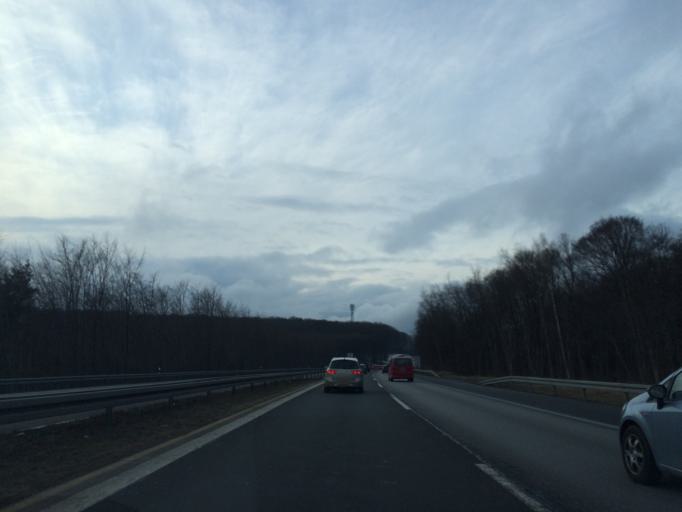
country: DE
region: Bavaria
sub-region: Regierungsbezirk Unterfranken
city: Bischbrunn
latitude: 49.8677
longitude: 9.4585
